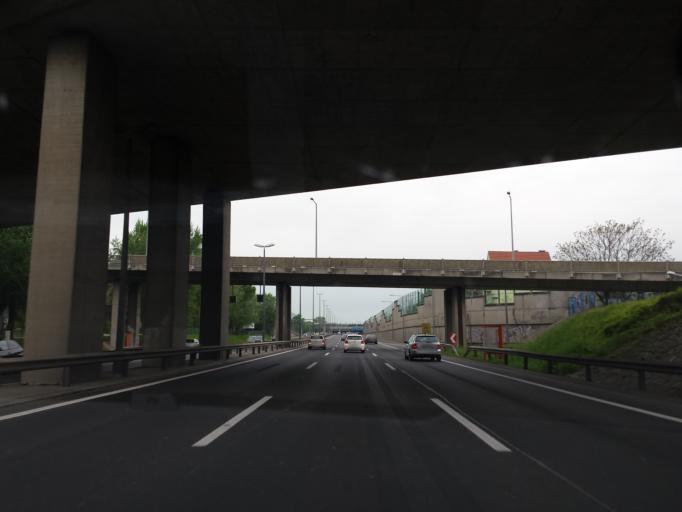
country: AT
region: Vienna
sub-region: Wien Stadt
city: Vienna
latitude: 48.2401
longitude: 16.4026
